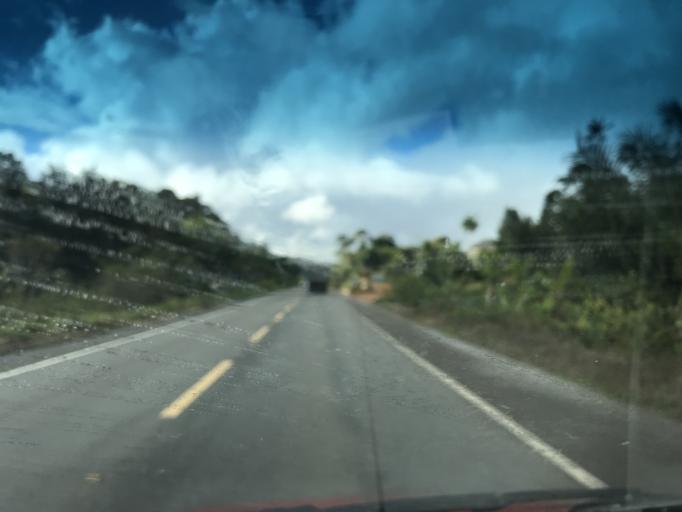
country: BR
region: Bahia
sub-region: Ibirataia
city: Ibirataia
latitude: -13.9693
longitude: -39.4786
